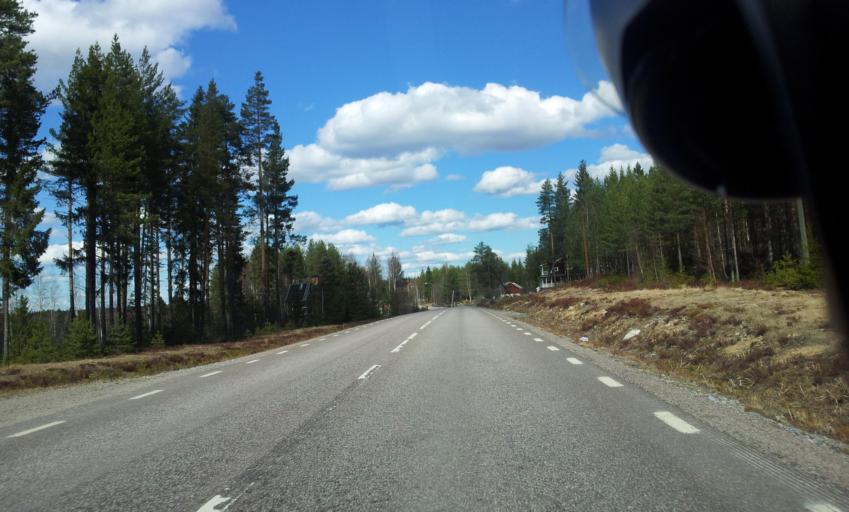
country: SE
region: Gaevleborg
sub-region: Ovanakers Kommun
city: Edsbyn
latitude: 61.2667
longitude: 15.8908
